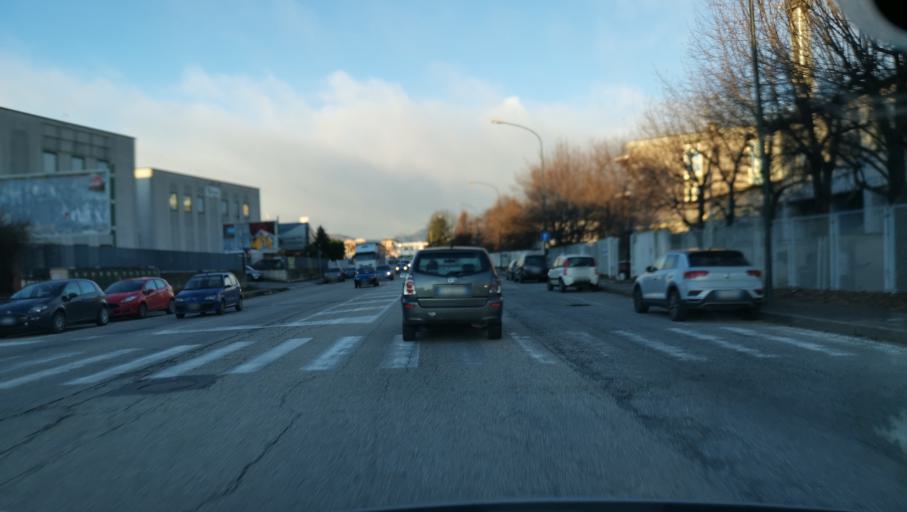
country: IT
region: Piedmont
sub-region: Provincia di Torino
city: Turin
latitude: 45.1110
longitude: 7.6729
